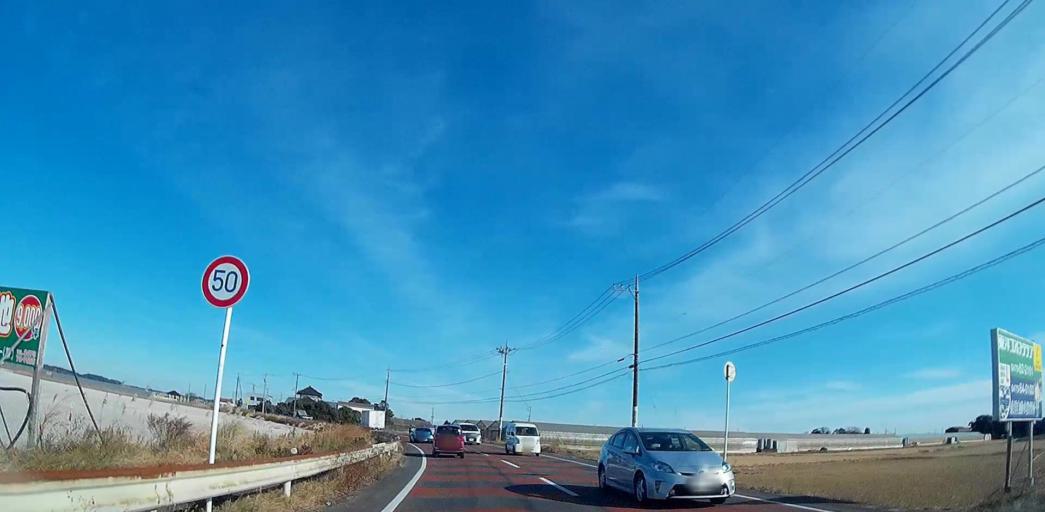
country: JP
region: Chiba
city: Asahi
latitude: 35.7407
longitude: 140.5983
